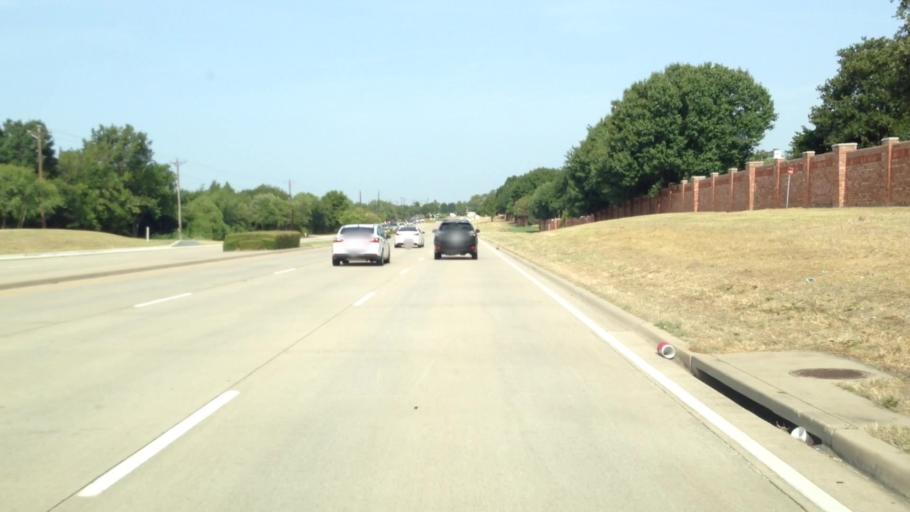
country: US
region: Texas
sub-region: Denton County
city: Lewisville
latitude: 33.0101
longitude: -97.0378
